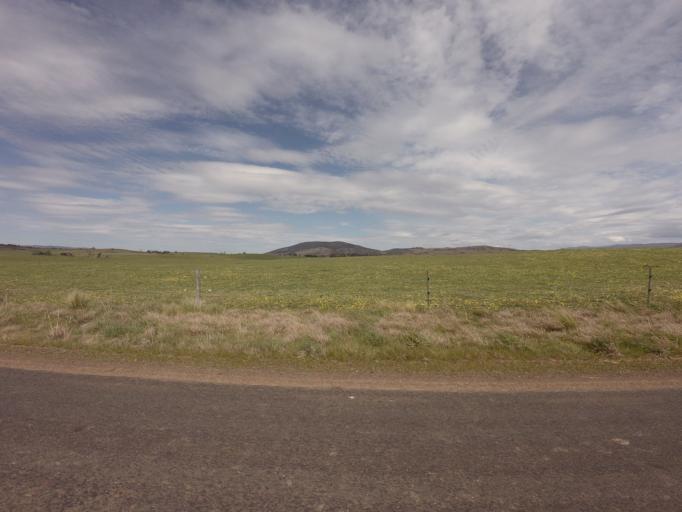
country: AU
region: Tasmania
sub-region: Northern Midlands
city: Evandale
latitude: -41.8869
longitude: 147.3788
